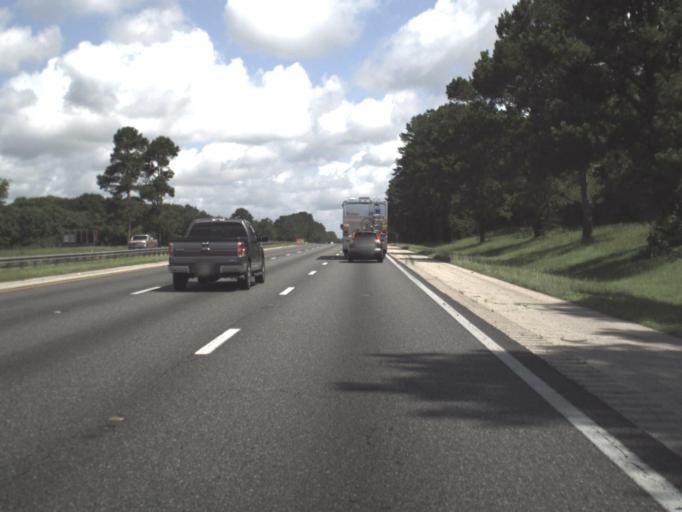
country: US
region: Florida
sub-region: Alachua County
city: High Springs
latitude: 29.8266
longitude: -82.5209
